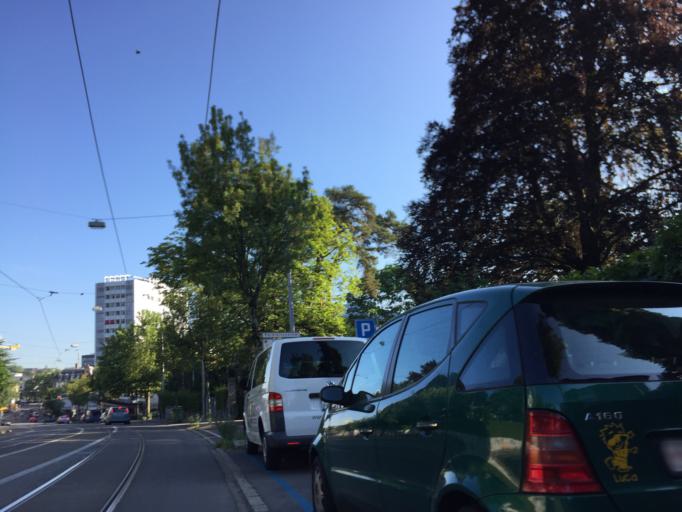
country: CH
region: Bern
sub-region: Bern-Mittelland District
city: Bern
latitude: 46.9389
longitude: 7.4322
